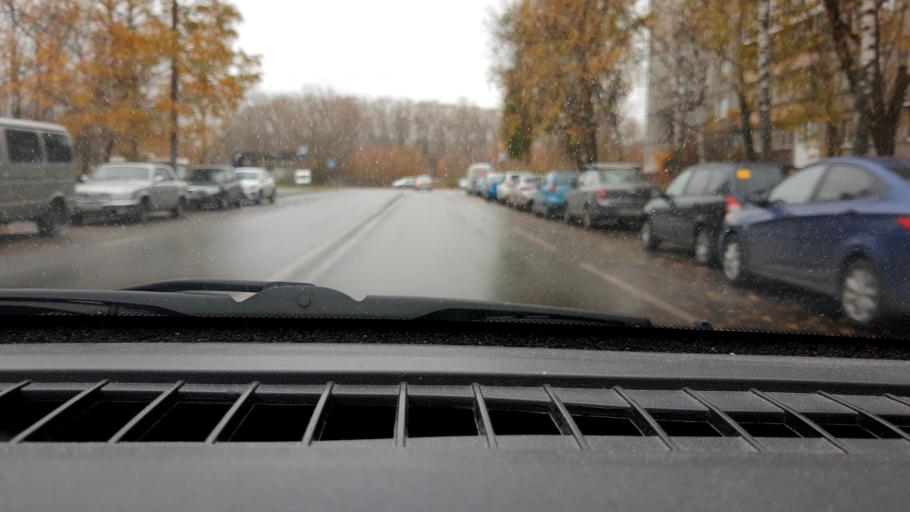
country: RU
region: Nizjnij Novgorod
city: Burevestnik
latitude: 56.2280
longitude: 43.8798
